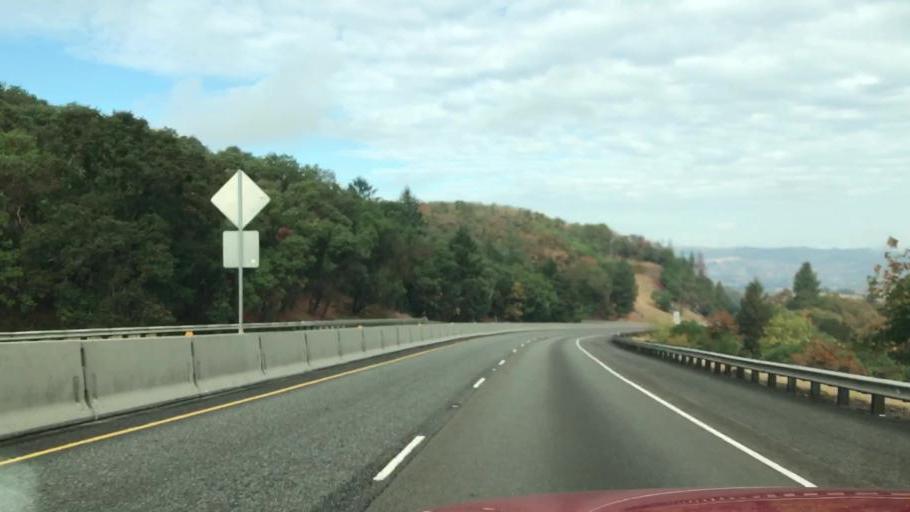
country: US
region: Oregon
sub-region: Douglas County
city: Green
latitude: 43.1137
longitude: -123.3566
